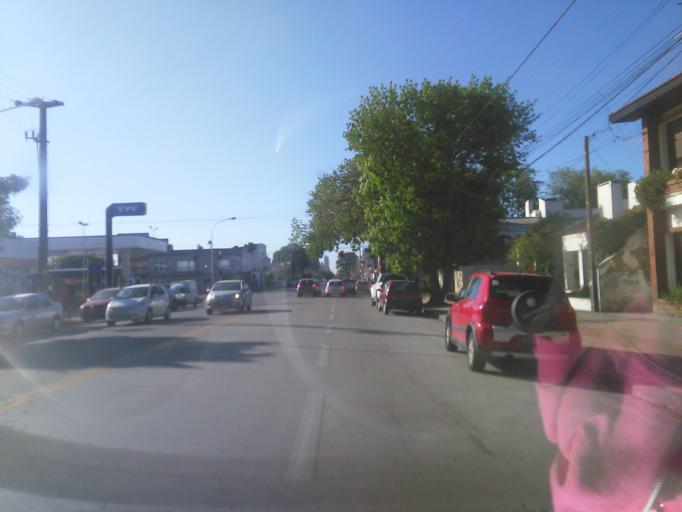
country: AR
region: Buenos Aires
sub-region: Partido de Tandil
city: Tandil
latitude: -37.3321
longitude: -59.1259
